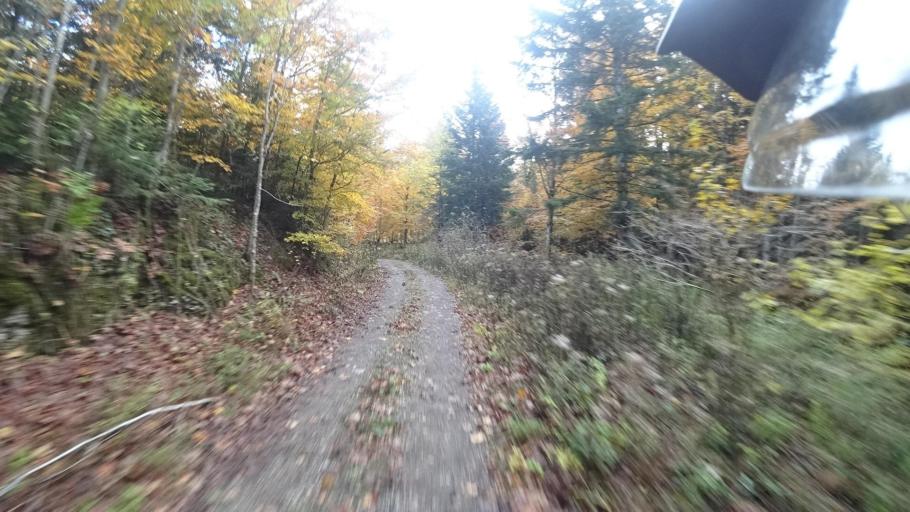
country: HR
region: Karlovacka
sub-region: Grad Ogulin
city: Ogulin
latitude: 45.2104
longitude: 15.0823
